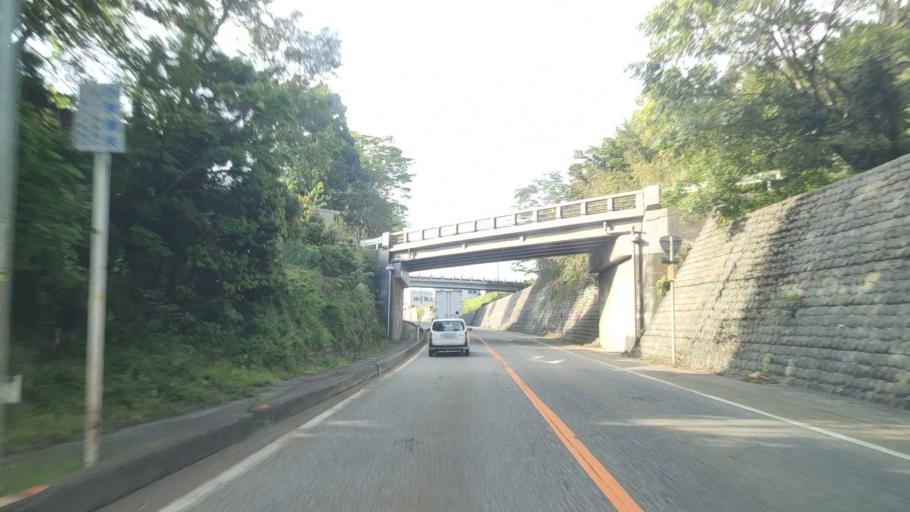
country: JP
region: Toyama
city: Yatsuomachi-higashikumisaka
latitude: 36.5585
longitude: 137.2154
